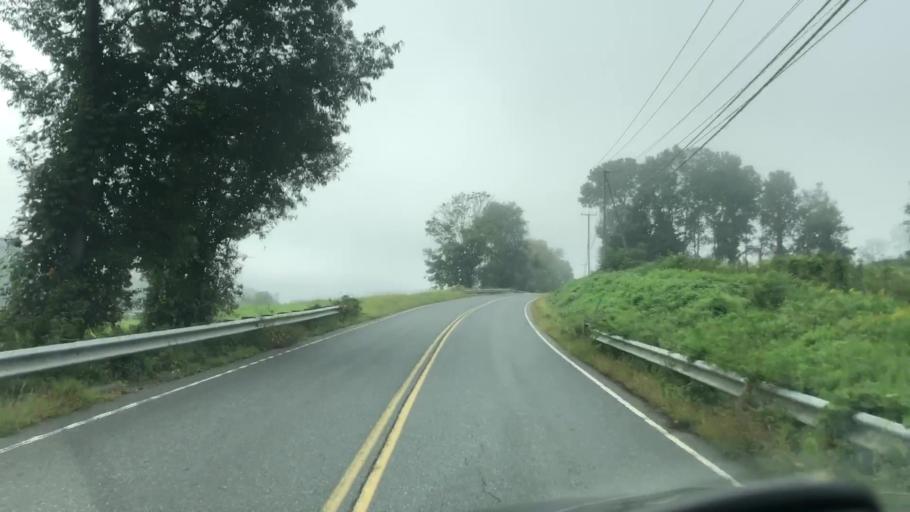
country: US
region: Massachusetts
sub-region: Franklin County
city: Northfield
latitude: 42.6736
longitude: -72.4796
